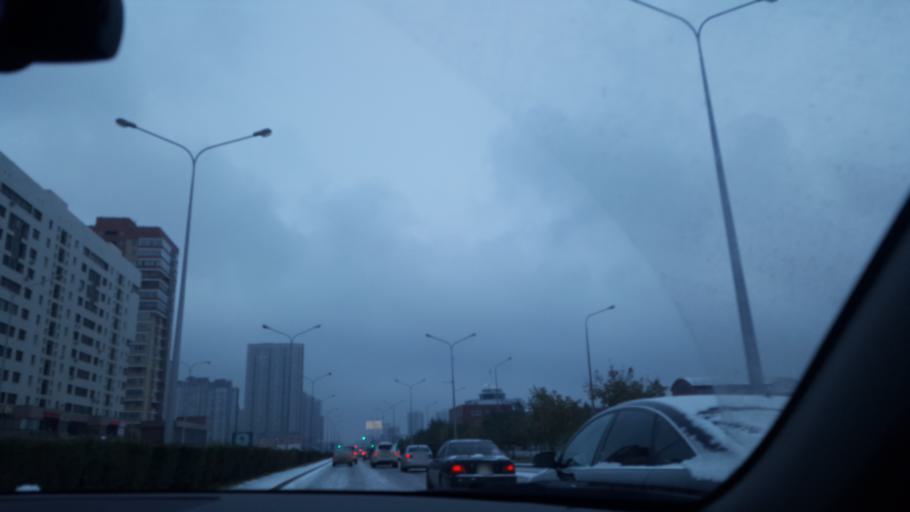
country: KZ
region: Astana Qalasy
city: Astana
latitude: 51.1260
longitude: 71.4808
